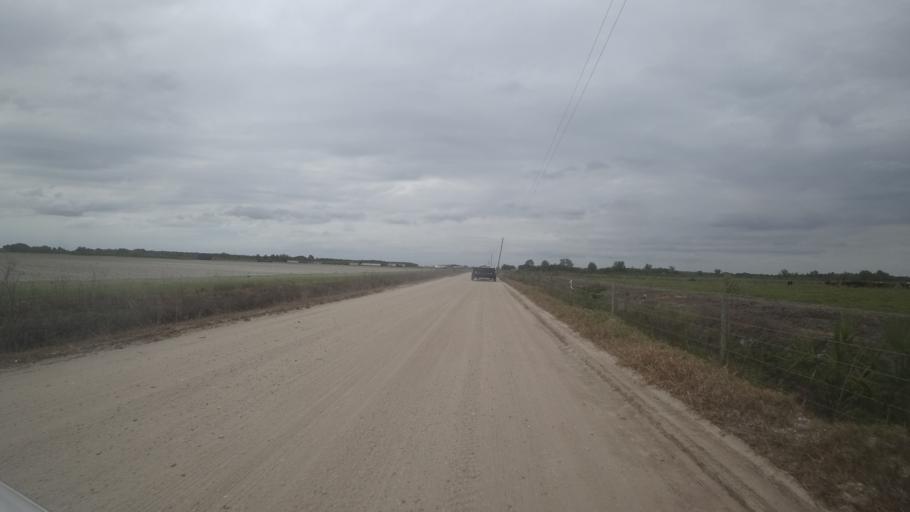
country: US
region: Florida
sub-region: Sarasota County
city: Warm Mineral Springs
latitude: 27.2750
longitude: -82.1700
